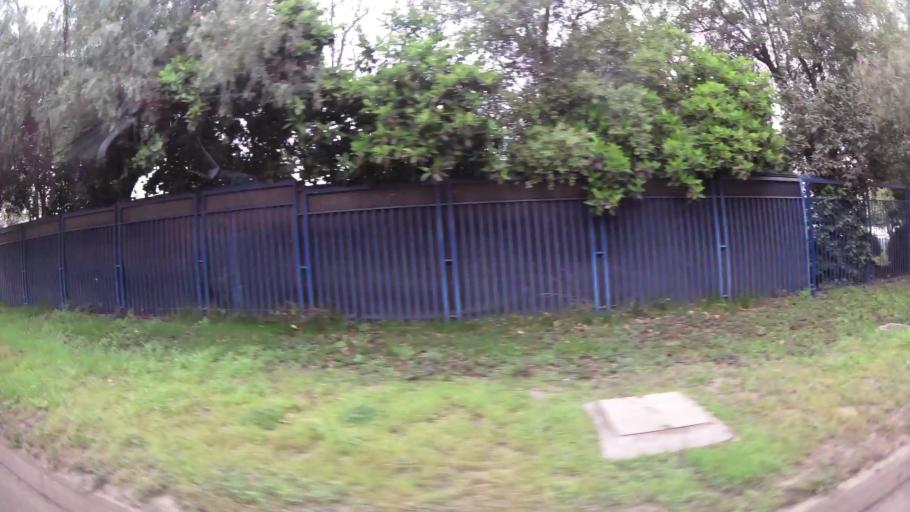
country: CL
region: Santiago Metropolitan
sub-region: Provincia de Chacabuco
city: Chicureo Abajo
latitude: -33.2185
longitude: -70.6637
